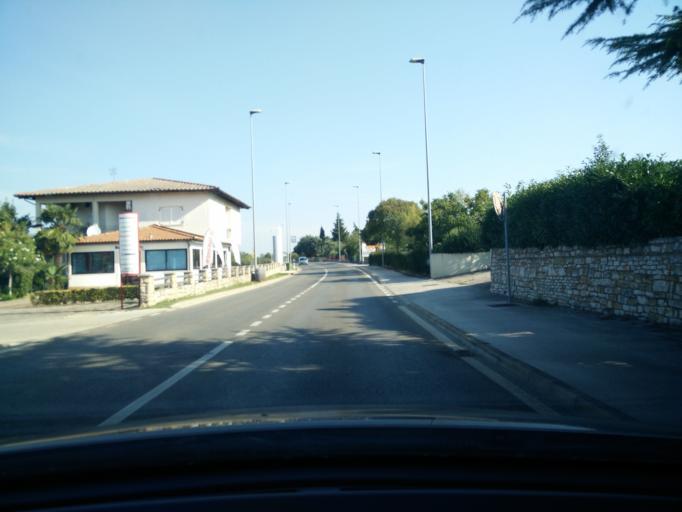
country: HR
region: Istarska
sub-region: Grad Porec
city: Porec
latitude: 45.2486
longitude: 13.6120
